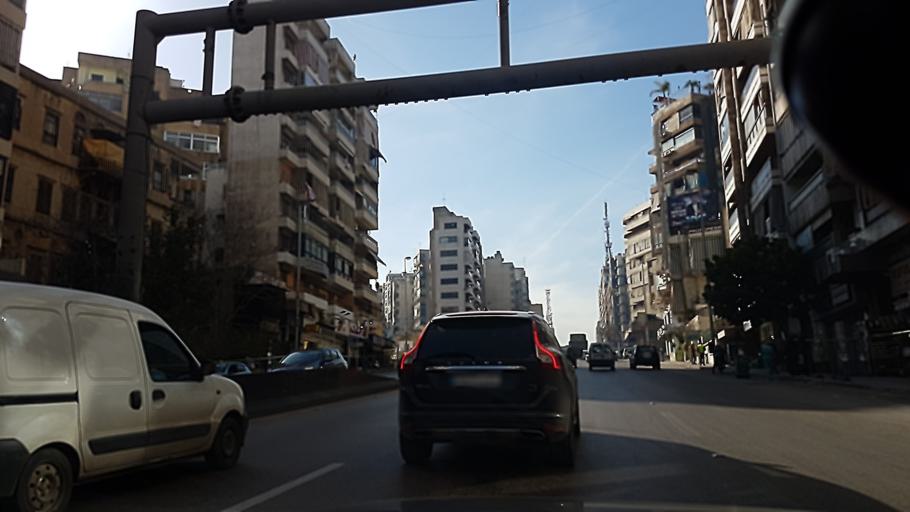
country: LB
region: Beyrouth
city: Beirut
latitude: 33.8898
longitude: 35.5000
